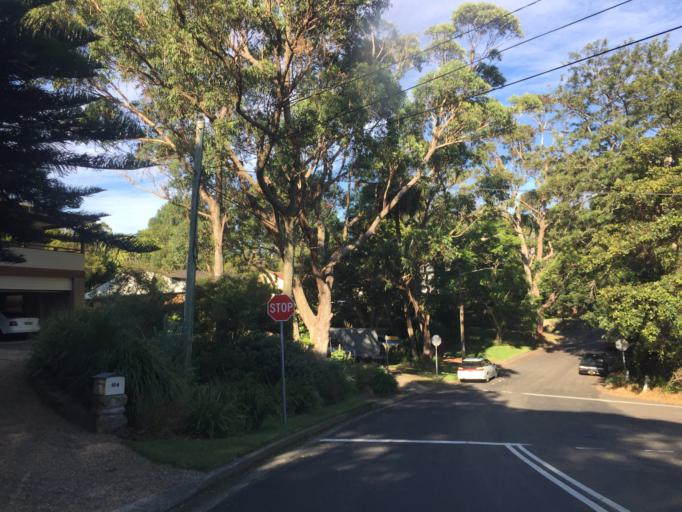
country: AU
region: New South Wales
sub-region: Pittwater
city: North Narrabeen
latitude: -33.7062
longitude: 151.2822
